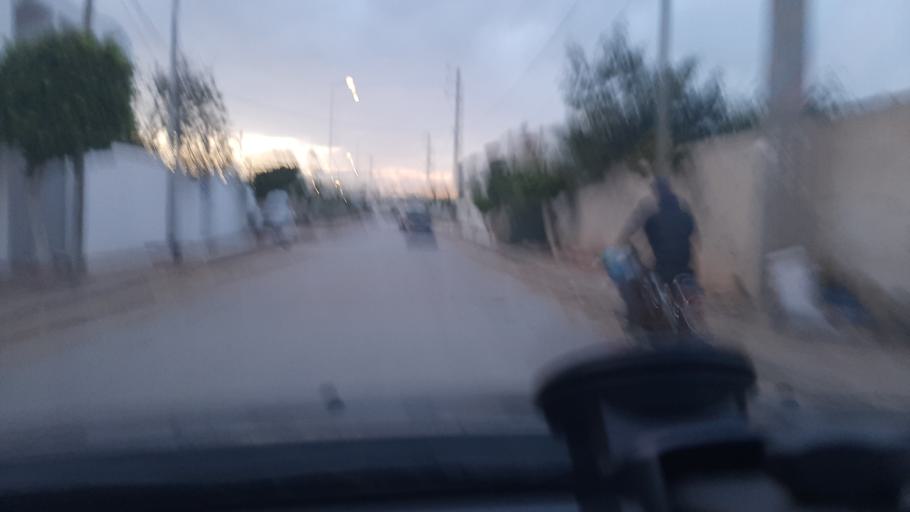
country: TN
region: Safaqis
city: Sfax
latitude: 34.7691
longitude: 10.7042
